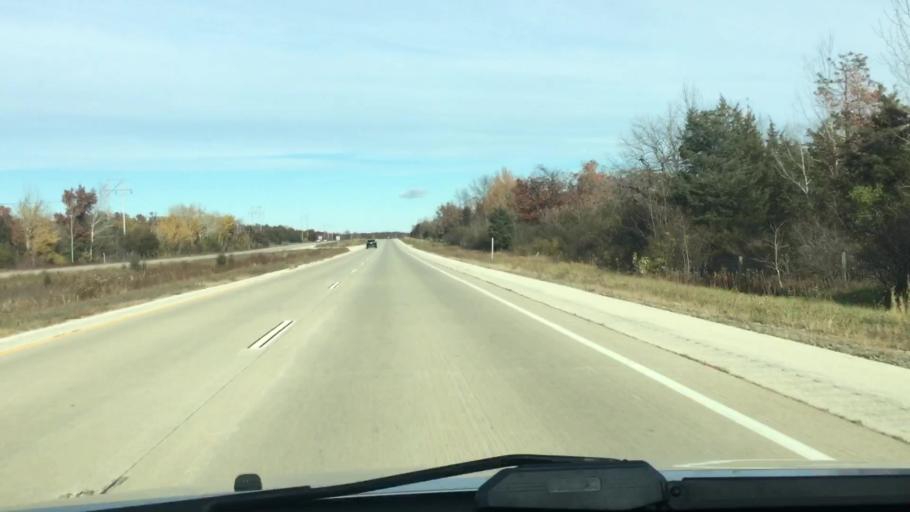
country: US
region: Wisconsin
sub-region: Kewaunee County
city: Luxemburg
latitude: 44.6243
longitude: -87.8190
